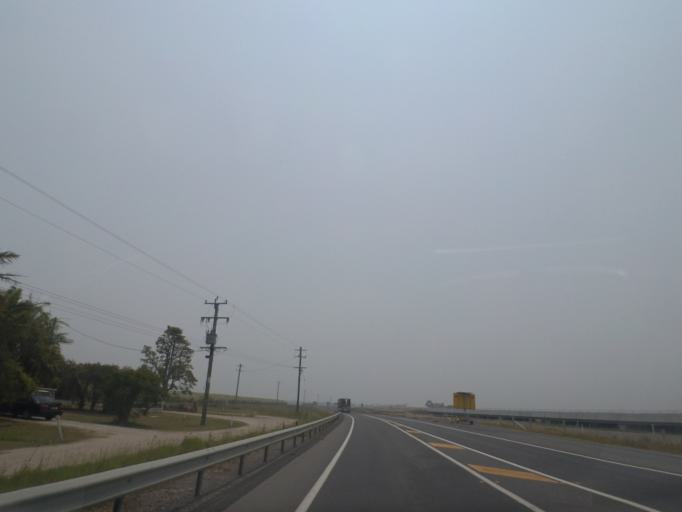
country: AU
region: New South Wales
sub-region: Clarence Valley
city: Maclean
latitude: -29.4174
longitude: 153.2410
